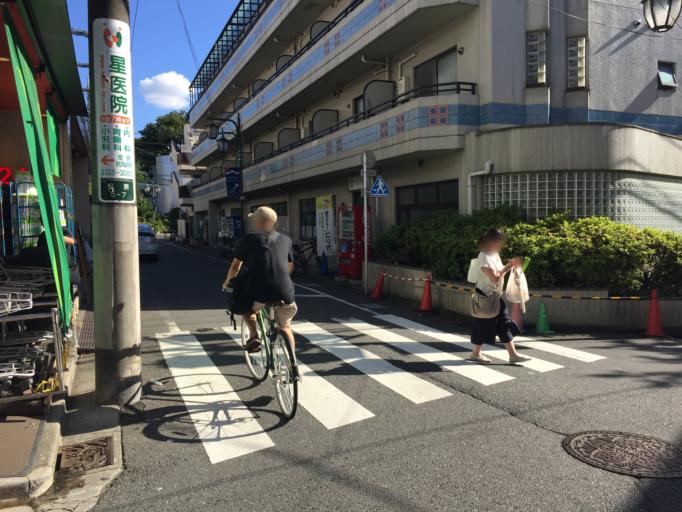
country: JP
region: Tokyo
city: Tokyo
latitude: 35.6618
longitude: 139.6543
